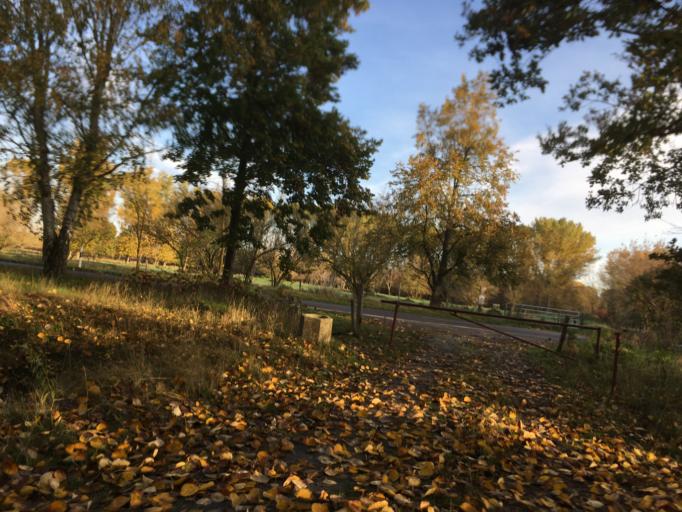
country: DE
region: Berlin
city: Buch
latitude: 52.6454
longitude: 13.4653
